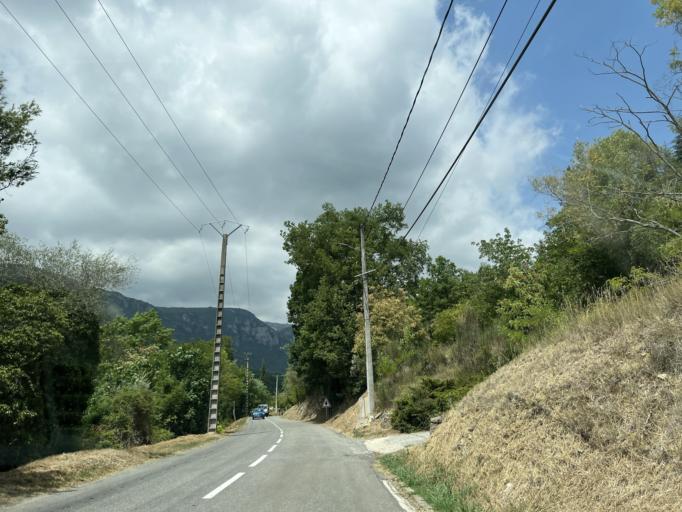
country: FR
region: Provence-Alpes-Cote d'Azur
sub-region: Departement des Alpes-Maritimes
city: Le Rouret
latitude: 43.7015
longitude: 7.0047
